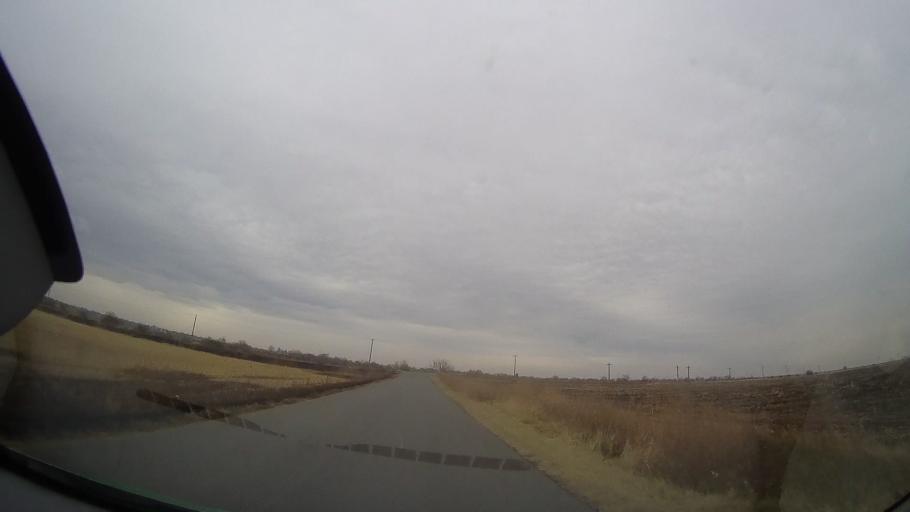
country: RO
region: Prahova
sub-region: Comuna Fantanele
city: Fantanele
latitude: 45.0090
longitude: 26.3562
